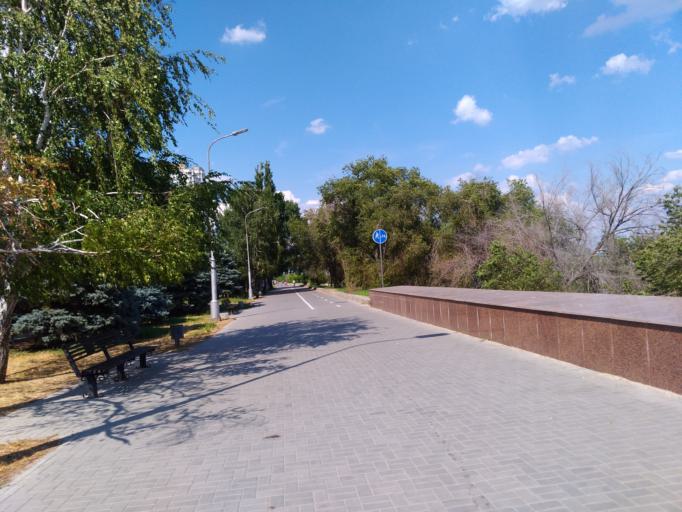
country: RU
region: Volgograd
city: Volgograd
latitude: 48.7163
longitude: 44.5354
